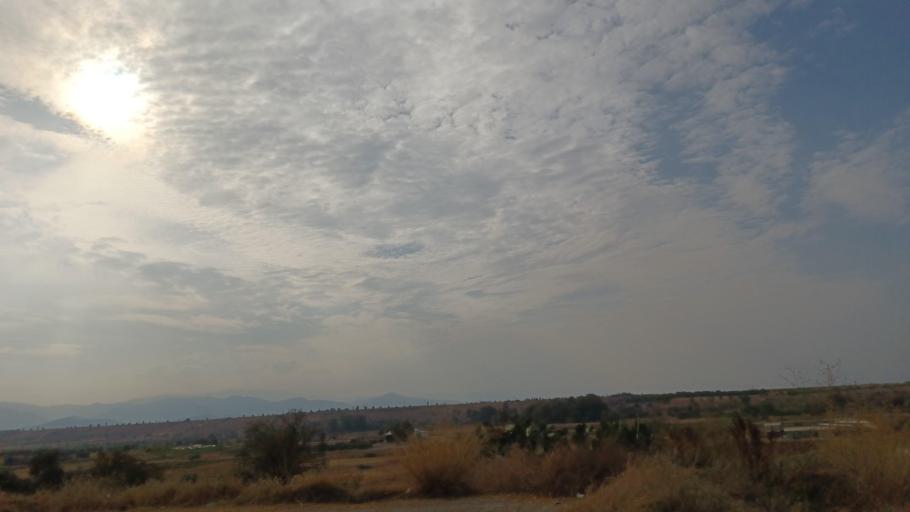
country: CY
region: Lefkosia
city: Peristerona
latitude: 35.1138
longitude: 33.0938
